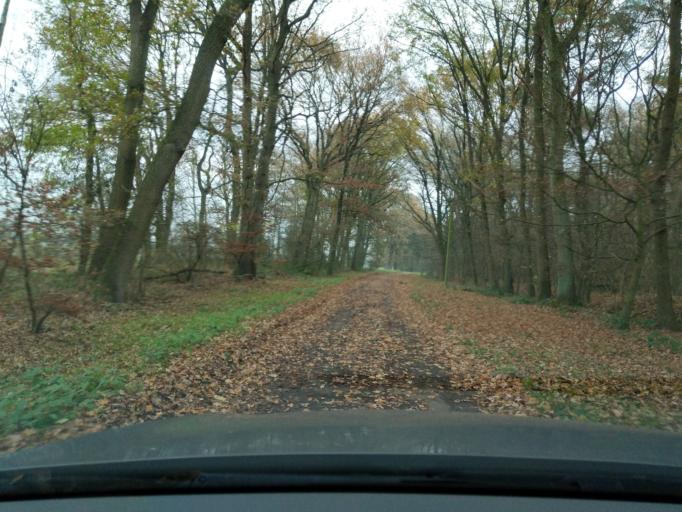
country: DE
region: Lower Saxony
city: Artlenburg
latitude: 53.3622
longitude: 10.4620
